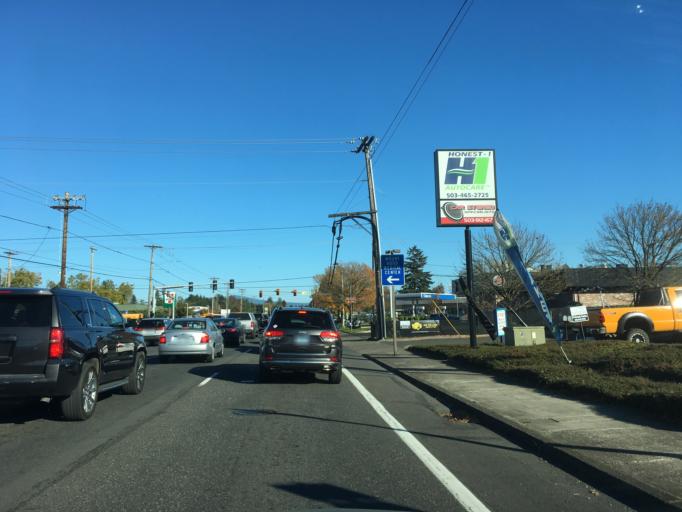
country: US
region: Oregon
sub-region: Multnomah County
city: Gresham
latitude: 45.5047
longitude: -122.4153
